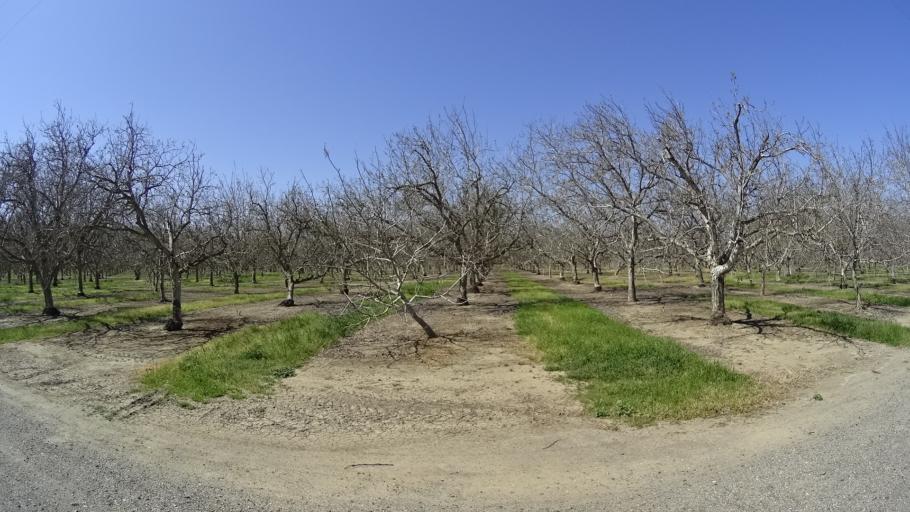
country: US
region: California
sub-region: Glenn County
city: Willows
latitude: 39.4460
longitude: -121.9869
